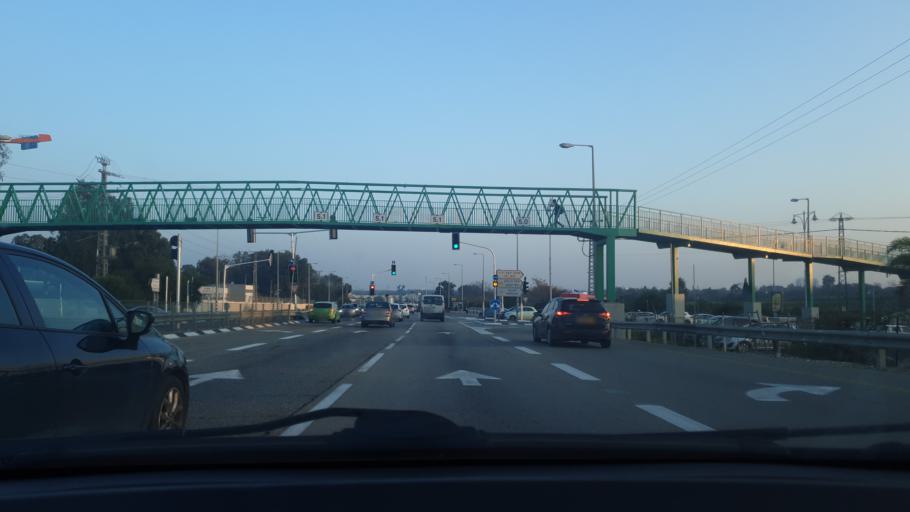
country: IL
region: Central District
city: Kefar Habad
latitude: 31.9697
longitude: 34.8433
